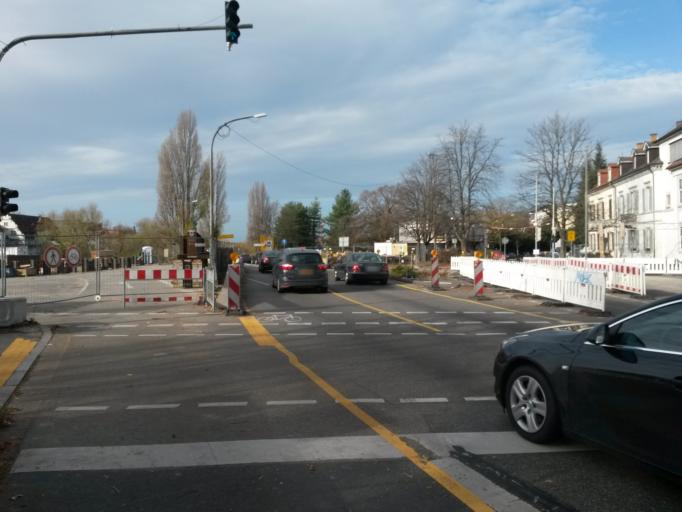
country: DE
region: Baden-Wuerttemberg
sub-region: Freiburg Region
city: Freiburg
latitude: 47.9907
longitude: 7.8455
